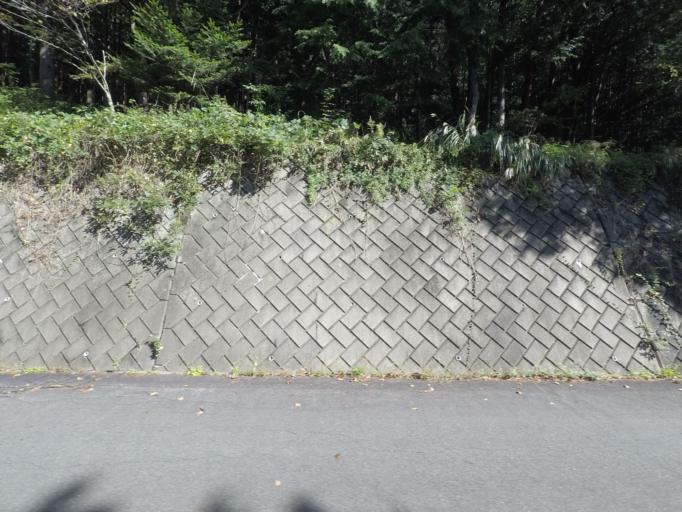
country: JP
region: Nagano
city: Tatsuno
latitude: 35.9743
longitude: 137.7571
